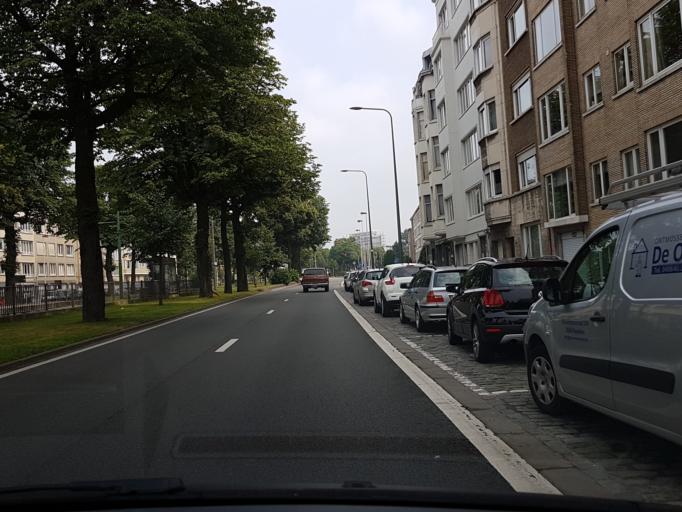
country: BE
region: Flanders
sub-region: Provincie Antwerpen
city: Antwerpen
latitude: 51.1851
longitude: 4.3919
